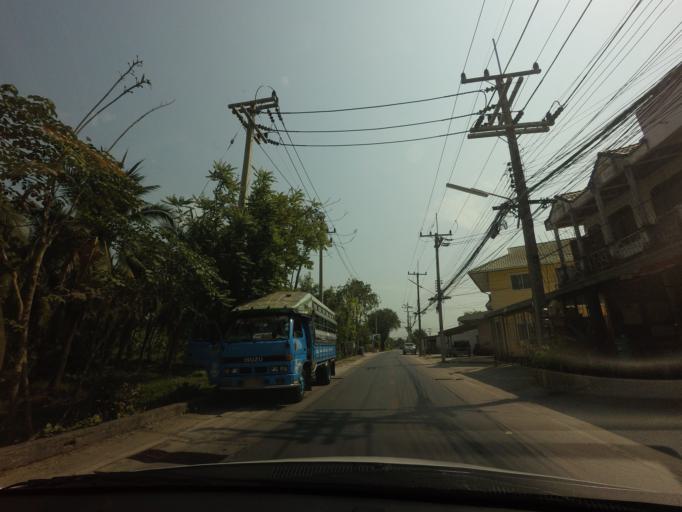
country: TH
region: Nakhon Pathom
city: Sam Phran
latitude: 13.6958
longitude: 100.2464
